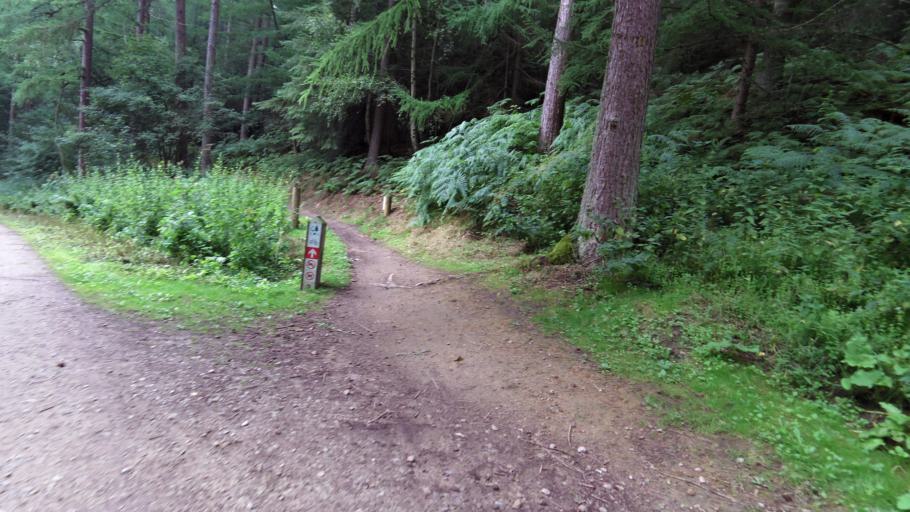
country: GB
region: England
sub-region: North Yorkshire
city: Thornton Dale
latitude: 54.2803
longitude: -0.6830
